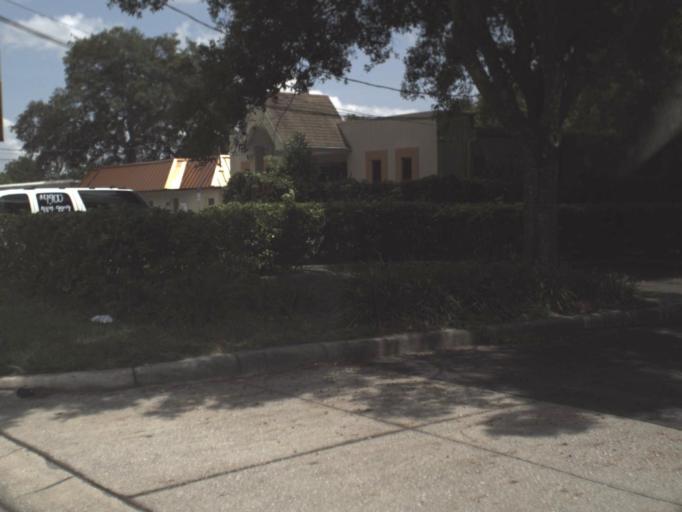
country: US
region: Florida
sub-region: Hillsborough County
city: Carrollwood
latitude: 28.0334
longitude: -82.4724
